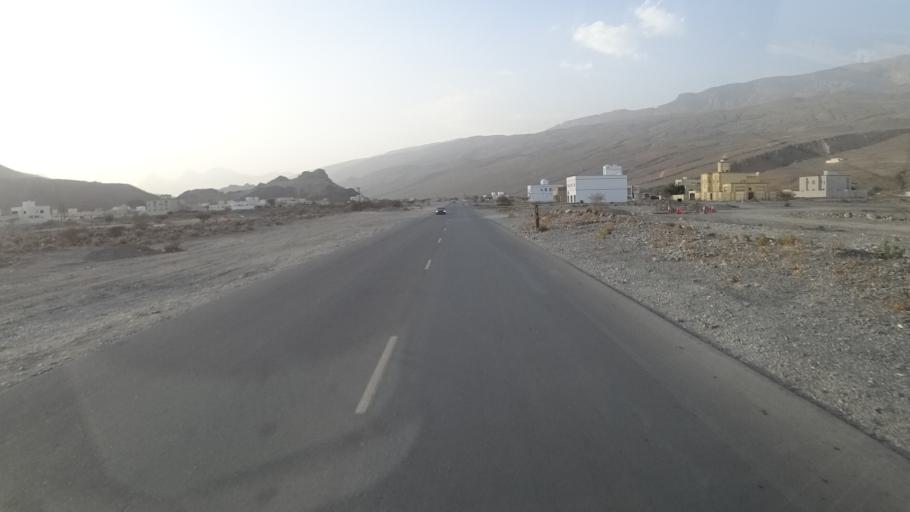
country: OM
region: Muhafazat ad Dakhiliyah
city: Bahla'
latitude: 23.1200
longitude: 57.2613
